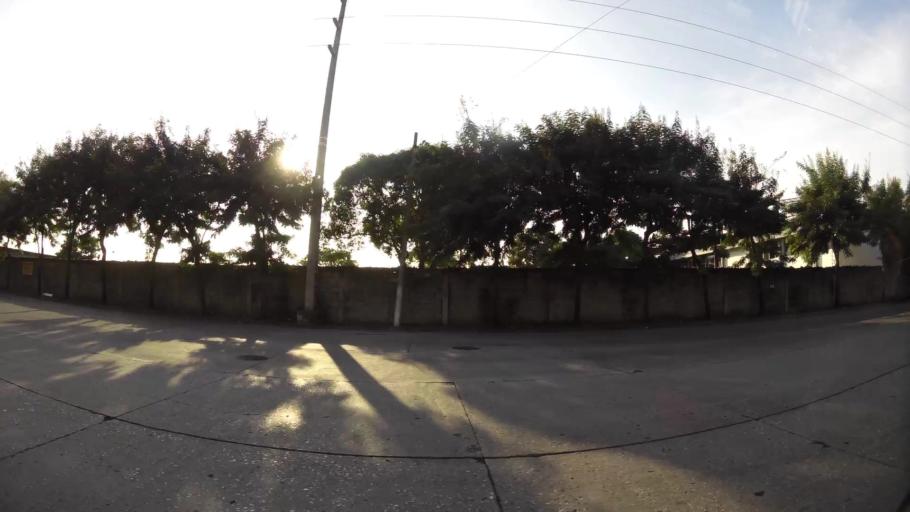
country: EC
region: Guayas
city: Eloy Alfaro
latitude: -2.1633
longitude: -79.8946
